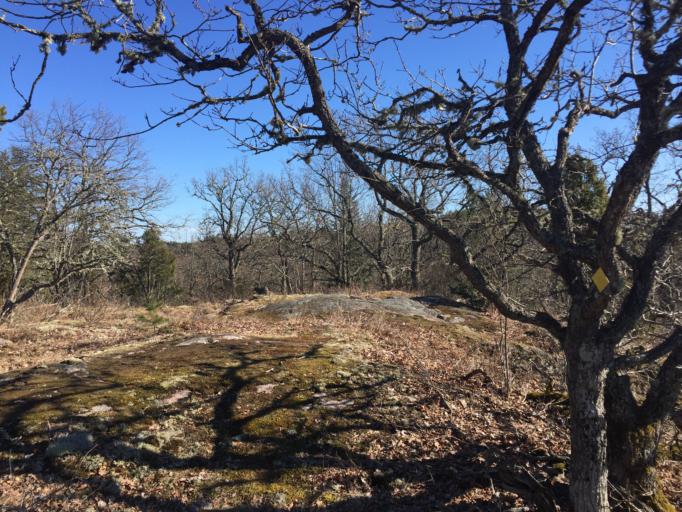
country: SE
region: Stockholm
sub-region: Nykvarns Kommun
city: Nykvarn
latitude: 59.2503
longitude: 17.3907
